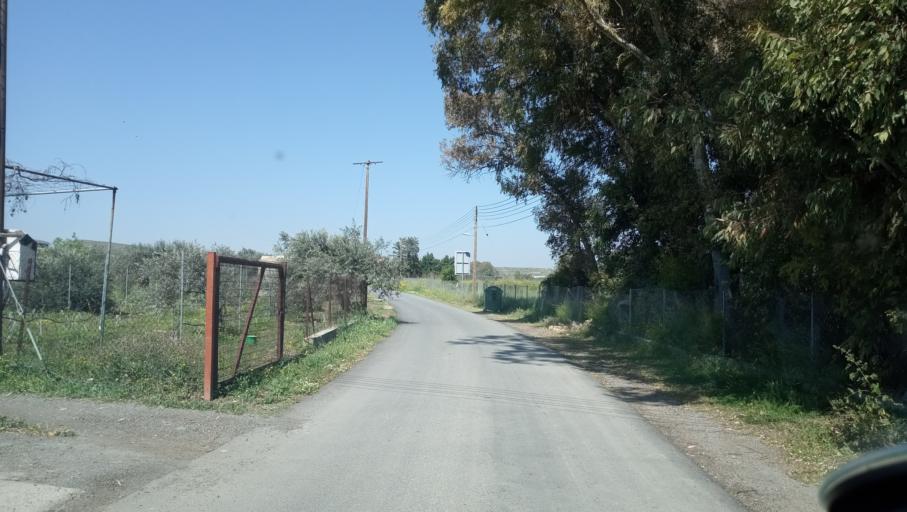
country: CY
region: Lefkosia
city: Alampra
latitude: 35.0156
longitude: 33.3864
